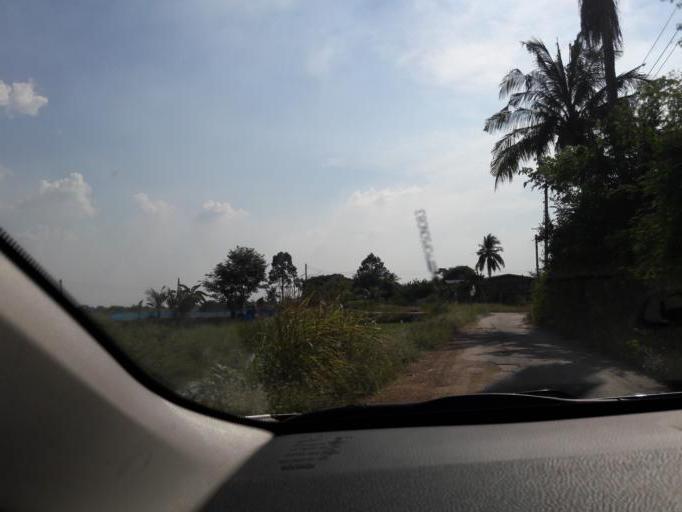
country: TH
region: Ang Thong
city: Wiset Chaichan
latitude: 14.5587
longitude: 100.3916
